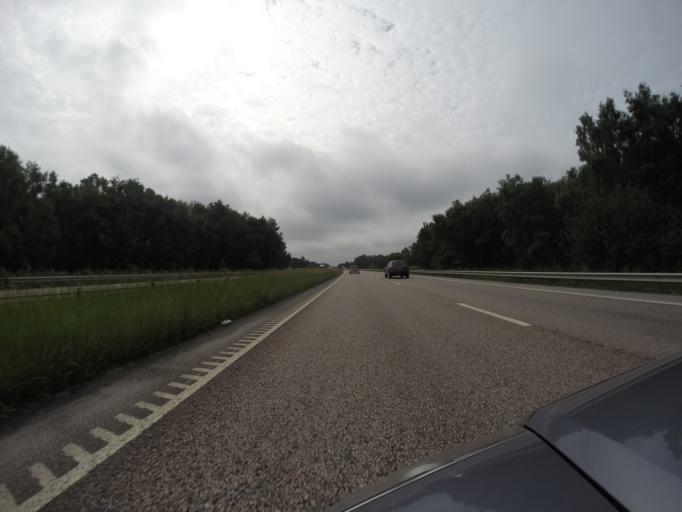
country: SE
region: Skane
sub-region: Kavlinge Kommun
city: Hofterup
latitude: 55.8158
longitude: 12.9406
